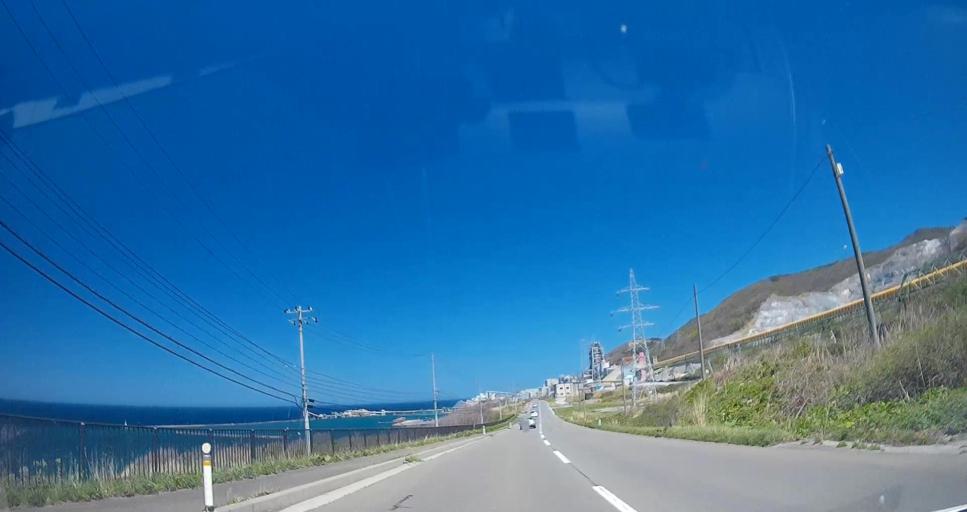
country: JP
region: Aomori
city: Mutsu
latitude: 41.4010
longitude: 141.4264
